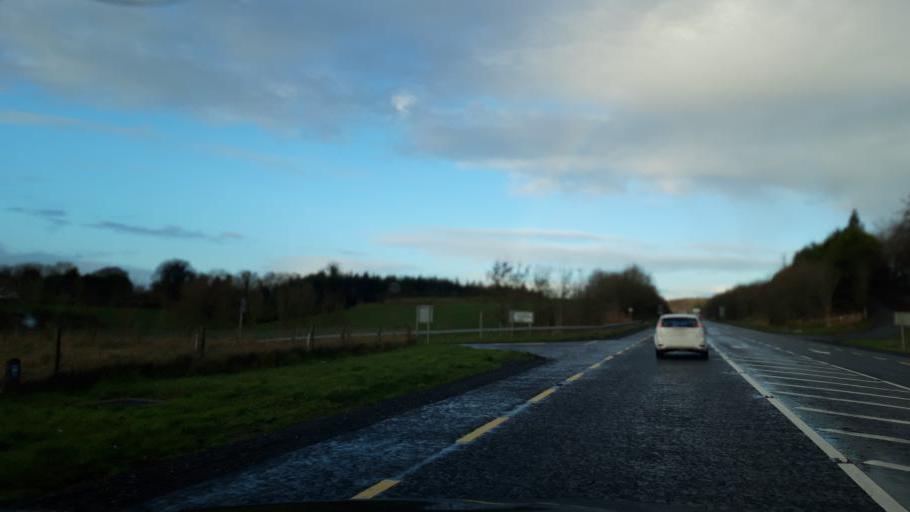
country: IE
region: Ulster
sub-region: County Monaghan
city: Carrickmacross
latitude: 54.0207
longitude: -6.7087
